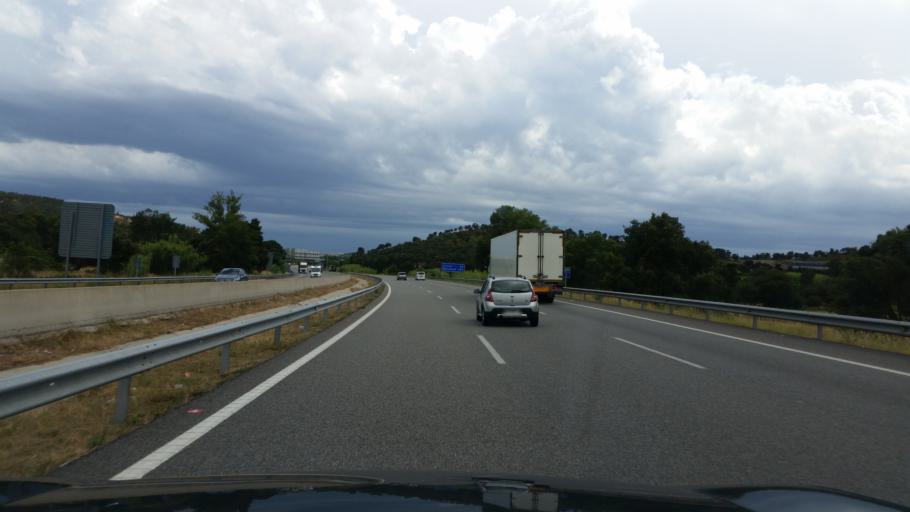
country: ES
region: Catalonia
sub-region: Provincia de Girona
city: la Jonquera
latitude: 42.3962
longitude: 2.8780
